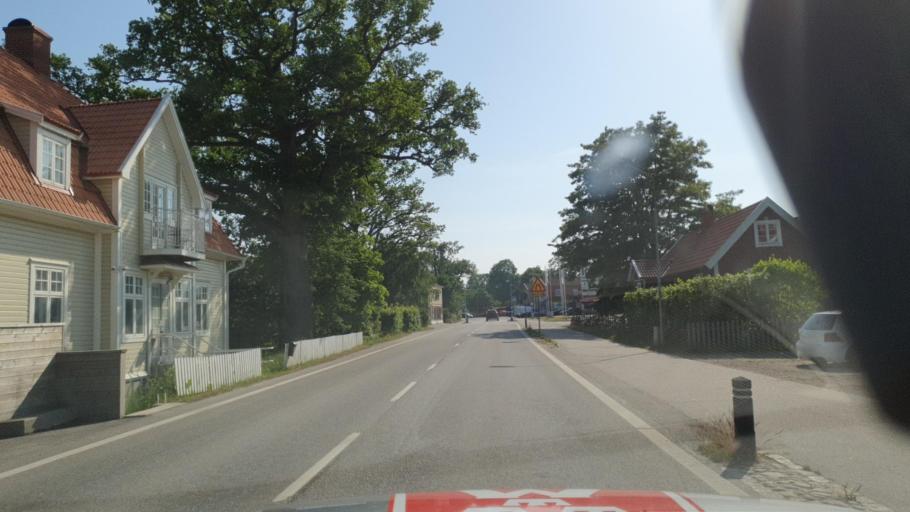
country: SE
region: Kalmar
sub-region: Kalmar Kommun
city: Ljungbyholm
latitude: 56.6348
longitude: 16.1766
